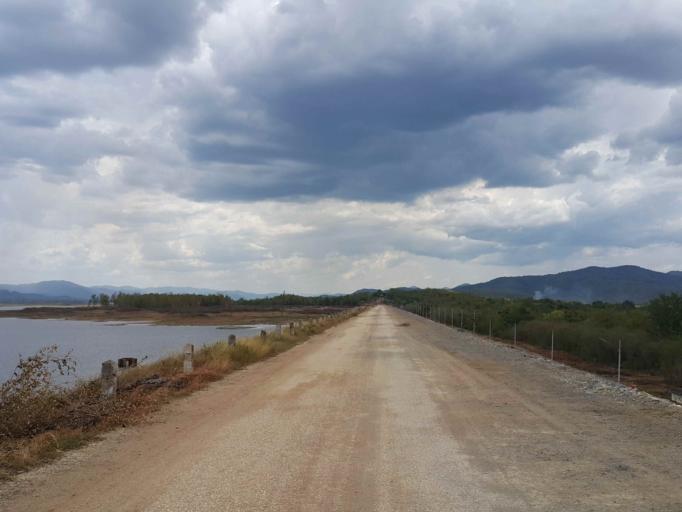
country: TH
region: Sukhothai
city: Thung Saliam
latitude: 17.3146
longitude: 99.4248
